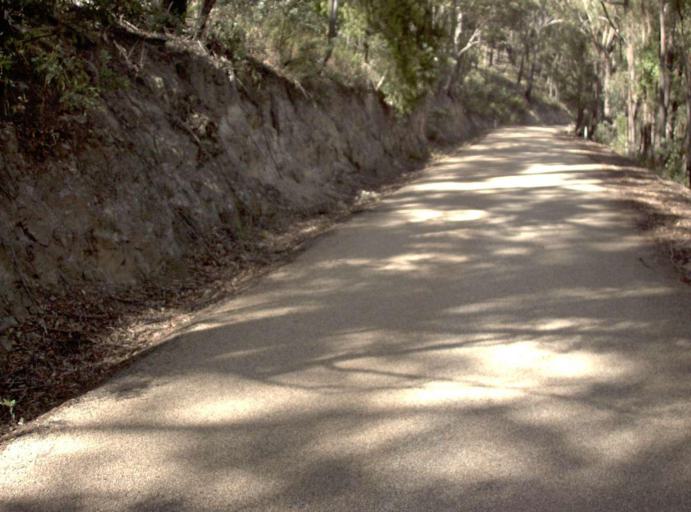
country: AU
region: Victoria
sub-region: East Gippsland
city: Lakes Entrance
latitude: -37.4039
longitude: 148.1270
